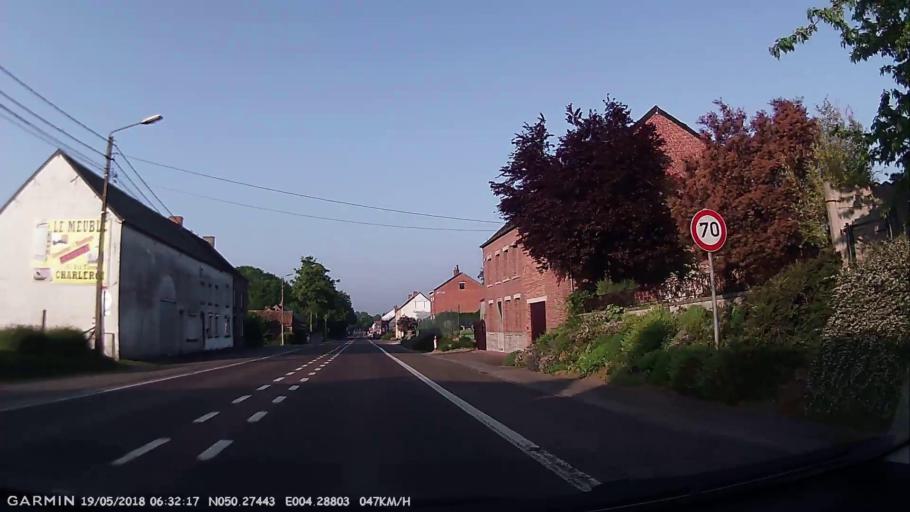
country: BE
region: Wallonia
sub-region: Province du Hainaut
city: Beaumont
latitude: 50.2744
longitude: 4.2880
